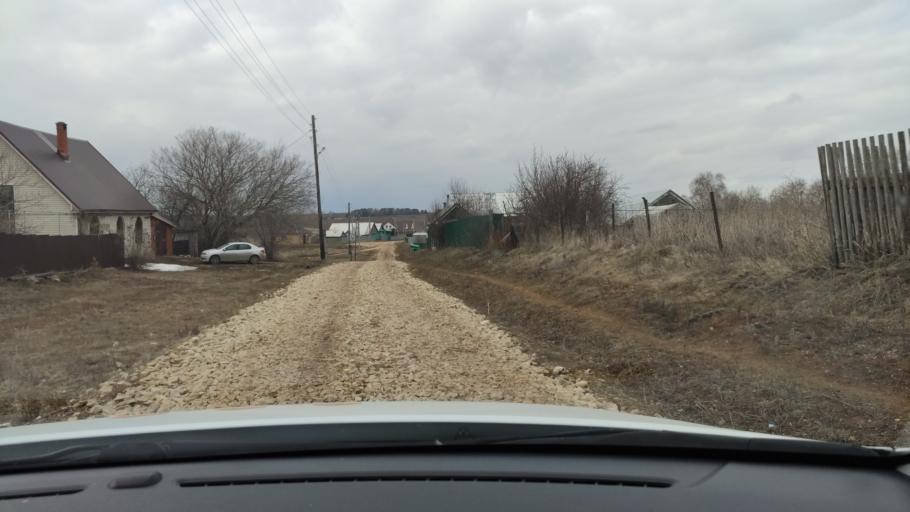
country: RU
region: Tatarstan
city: Vysokaya Gora
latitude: 56.2089
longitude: 49.3152
